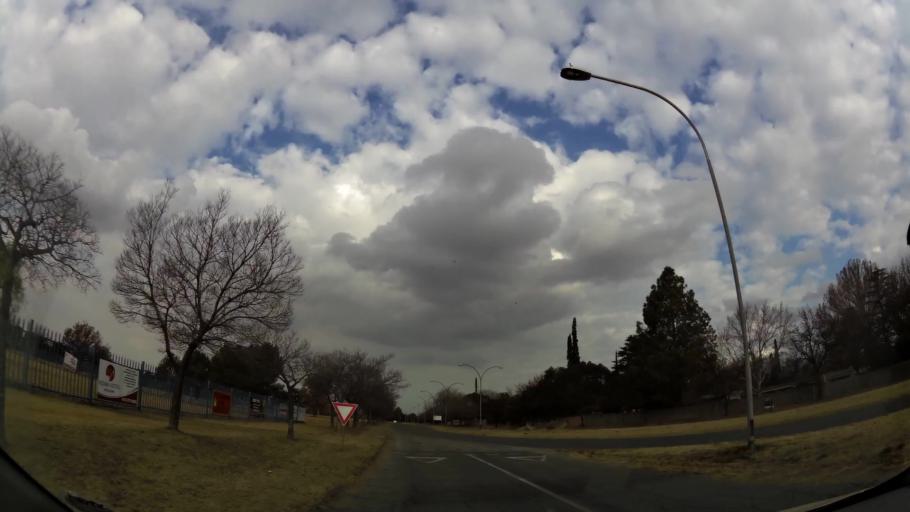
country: ZA
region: Orange Free State
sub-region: Fezile Dabi District Municipality
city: Sasolburg
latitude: -26.7962
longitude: 27.8249
